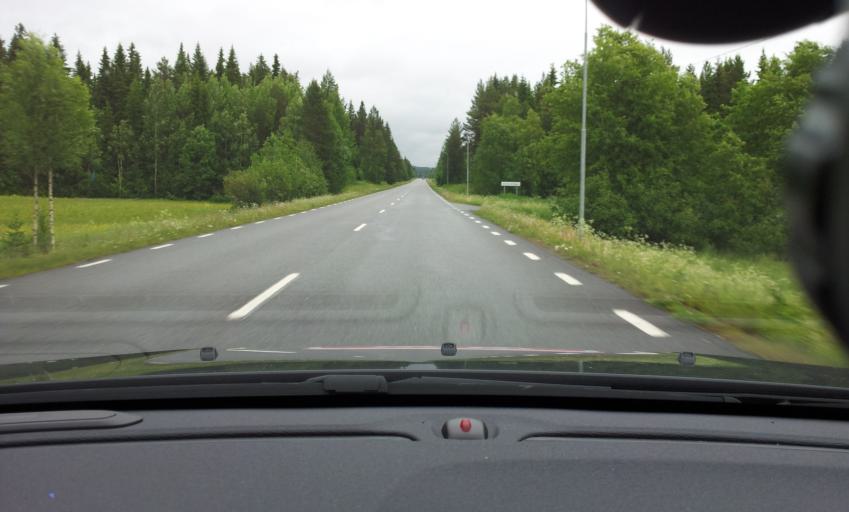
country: SE
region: Jaemtland
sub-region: Stroemsunds Kommun
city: Stroemsund
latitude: 63.5479
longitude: 15.4076
